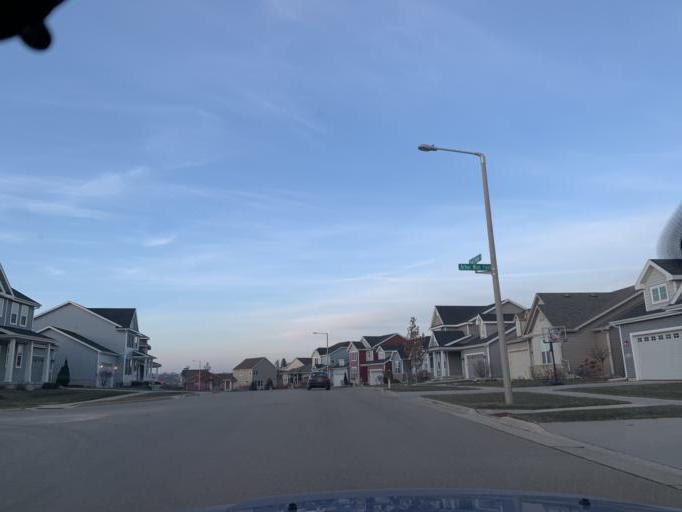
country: US
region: Wisconsin
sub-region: Dane County
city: Middleton
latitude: 43.0562
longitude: -89.5626
